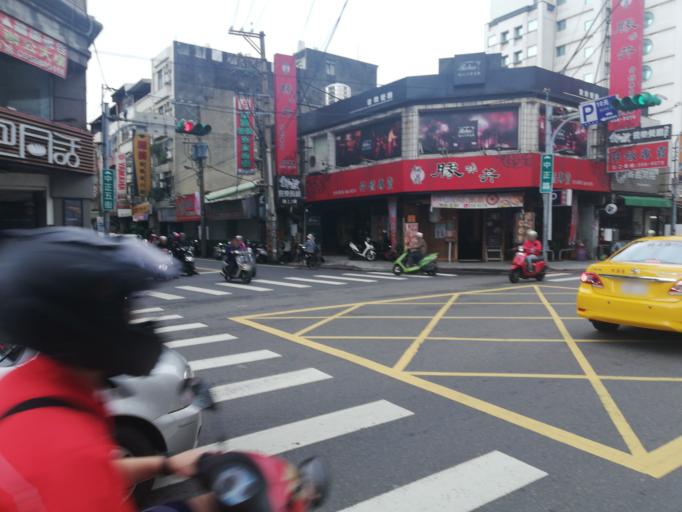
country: TW
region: Taiwan
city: Taoyuan City
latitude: 25.0064
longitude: 121.3036
